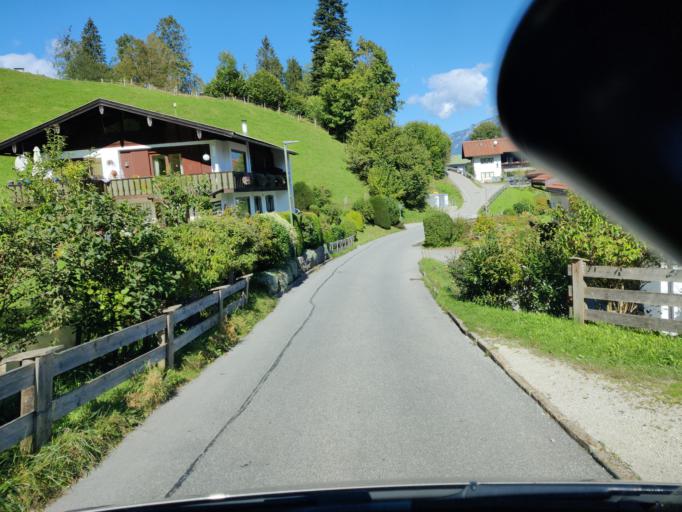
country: DE
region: Bavaria
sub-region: Upper Bavaria
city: Schoenau am Koenigssee
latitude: 47.5926
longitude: 12.9839
